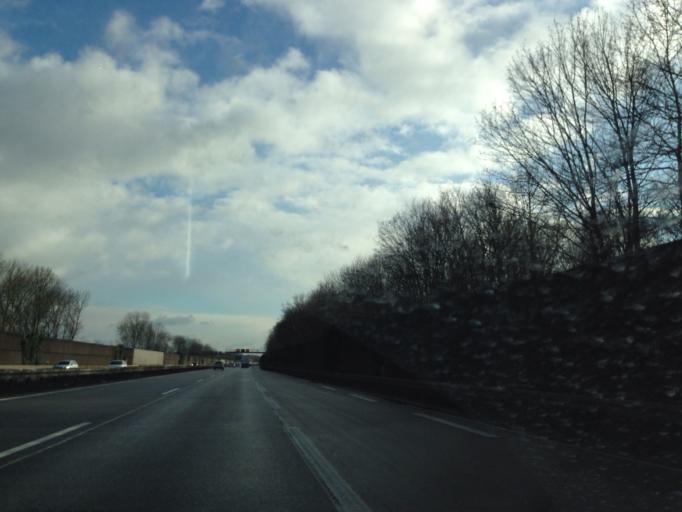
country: DE
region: North Rhine-Westphalia
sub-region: Regierungsbezirk Dusseldorf
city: Krefeld
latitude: 51.3650
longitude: 6.6263
